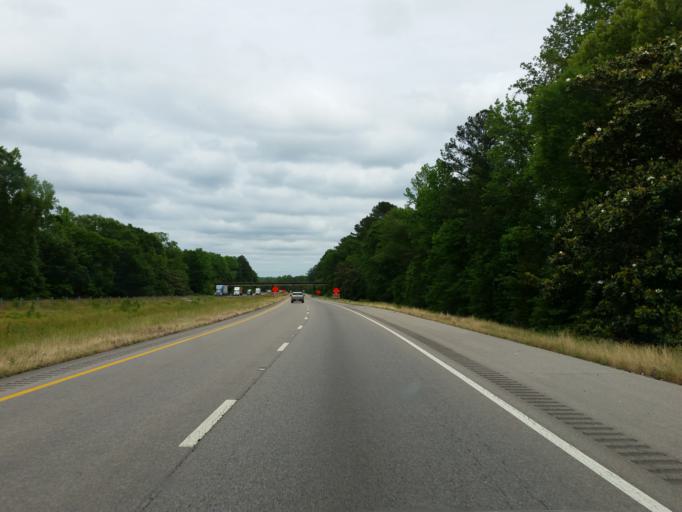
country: US
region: Mississippi
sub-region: Lauderdale County
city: Marion
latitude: 32.4107
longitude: -88.4734
